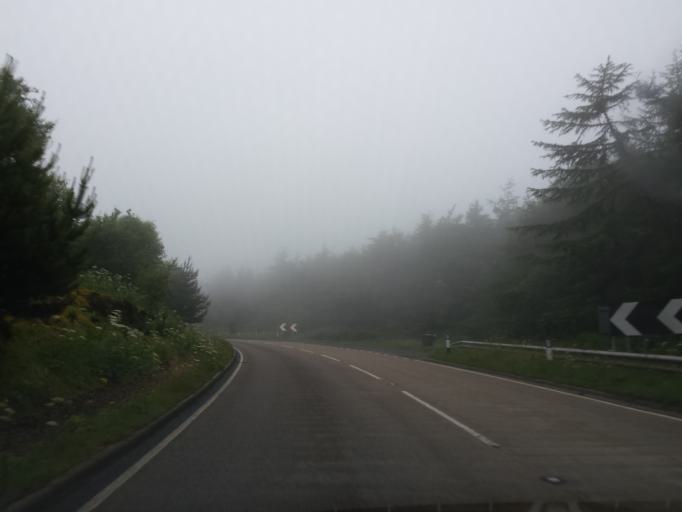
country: GB
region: Scotland
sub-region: Highland
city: Brora
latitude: 58.1777
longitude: -3.5159
